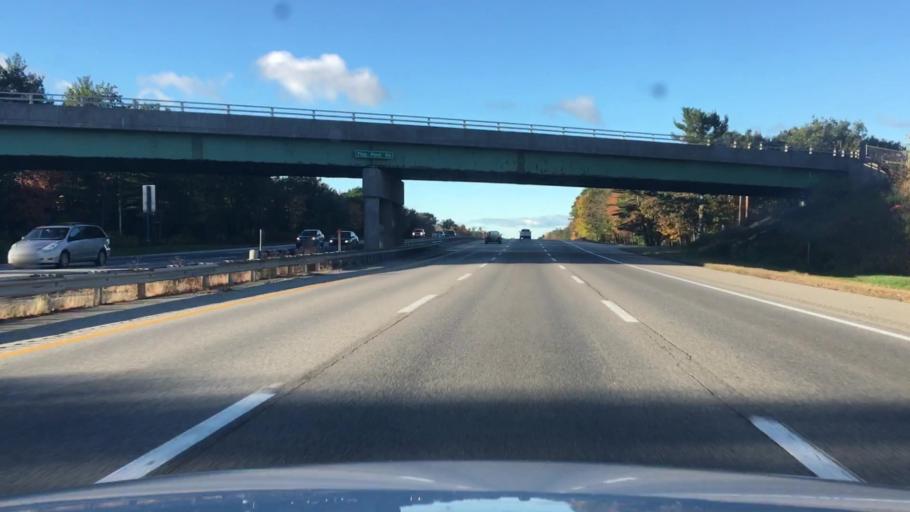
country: US
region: Maine
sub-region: Cumberland County
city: West Scarborough
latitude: 43.5543
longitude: -70.4247
